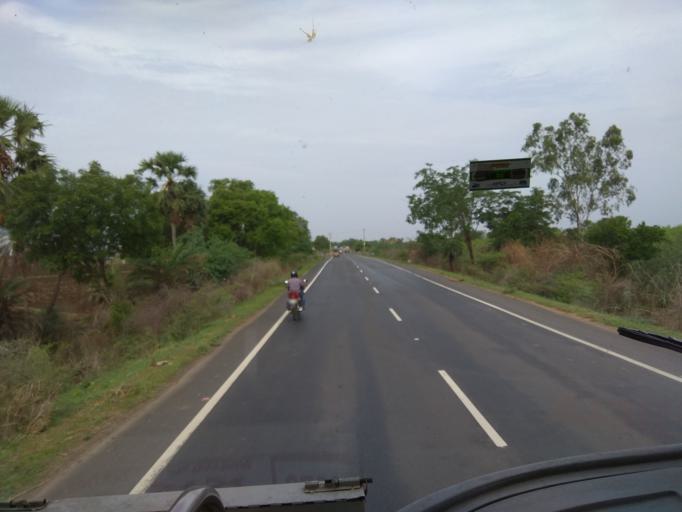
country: IN
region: Andhra Pradesh
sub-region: Guntur
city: Phirangipuram
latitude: 16.2842
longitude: 80.2256
